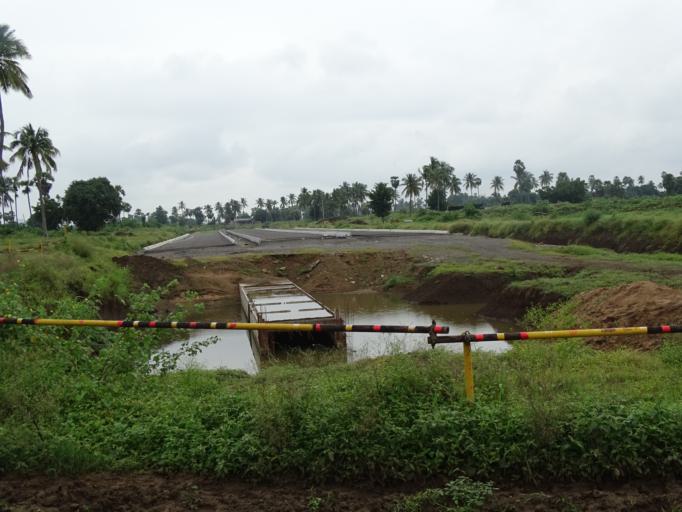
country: IN
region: Andhra Pradesh
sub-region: Krishna
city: Kondapalle
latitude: 16.5550
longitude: 80.4842
